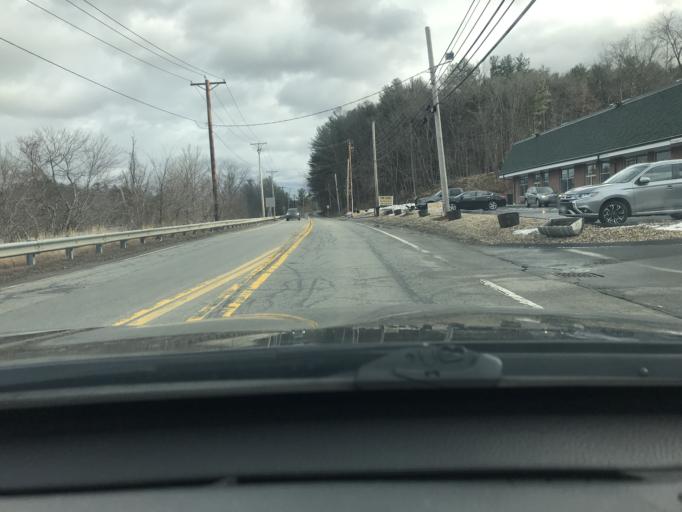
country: US
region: Massachusetts
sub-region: Middlesex County
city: Tyngsboro
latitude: 42.6710
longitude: -71.4199
